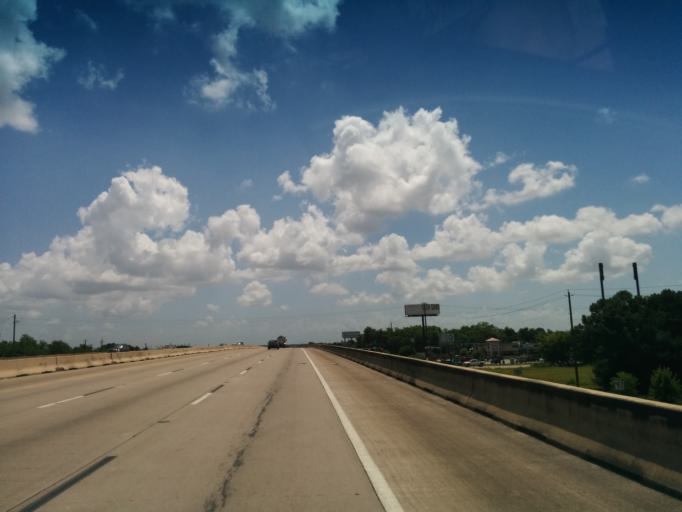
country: US
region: Texas
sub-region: Harris County
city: Baytown
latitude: 29.8075
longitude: -94.9670
